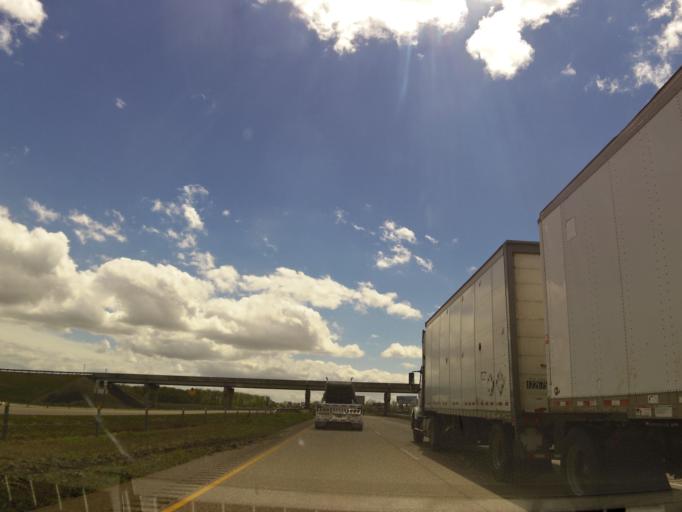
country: US
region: Arkansas
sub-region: Crittenden County
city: Marion
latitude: 35.3668
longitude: -90.2798
